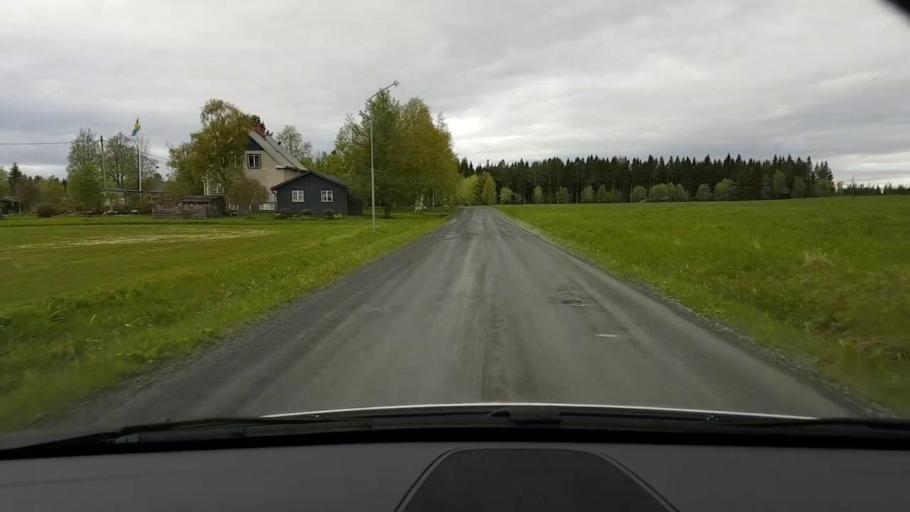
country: SE
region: Jaemtland
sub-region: Krokoms Kommun
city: Valla
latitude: 63.3061
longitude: 14.0038
